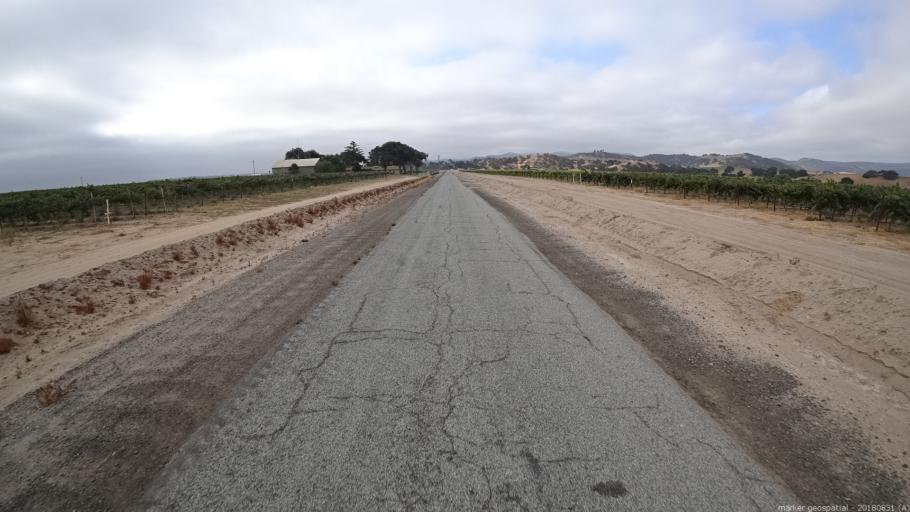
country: US
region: California
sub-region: Monterey County
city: King City
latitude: 36.1492
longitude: -121.1005
